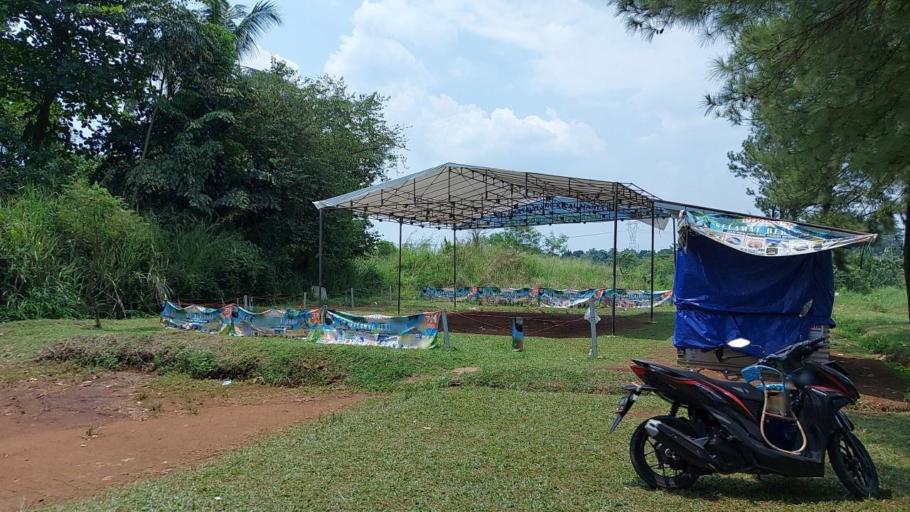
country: ID
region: West Java
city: Cibinong
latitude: -6.5090
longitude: 106.7791
